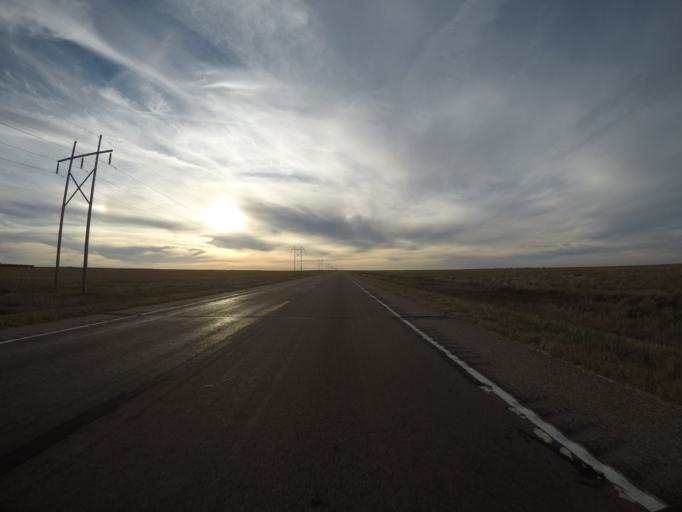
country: US
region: Colorado
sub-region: Yuma County
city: Yuma
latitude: 39.6554
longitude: -102.7657
